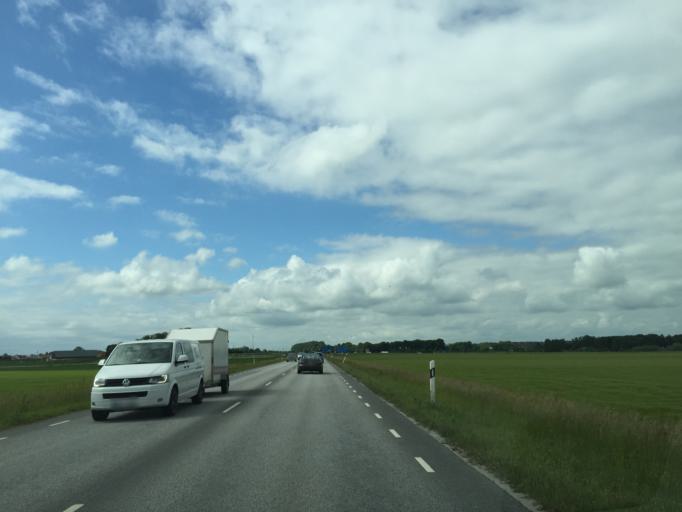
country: SE
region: Skane
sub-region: Lunds Kommun
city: Lund
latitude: 55.6737
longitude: 13.1896
